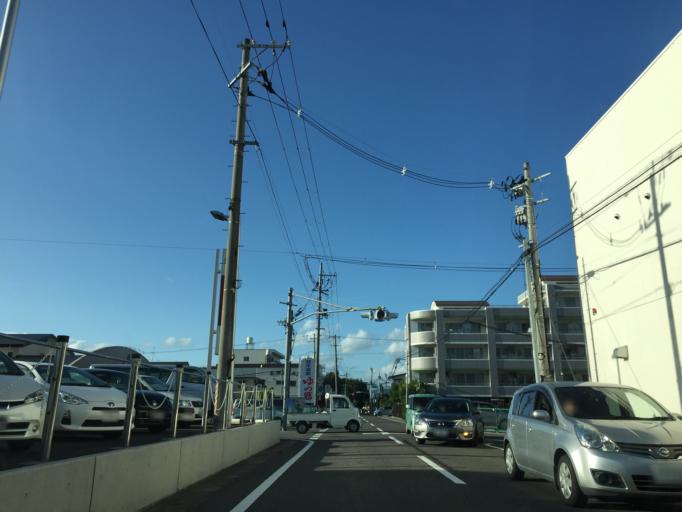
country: JP
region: Fukushima
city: Koriyama
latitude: 37.4082
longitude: 140.3591
